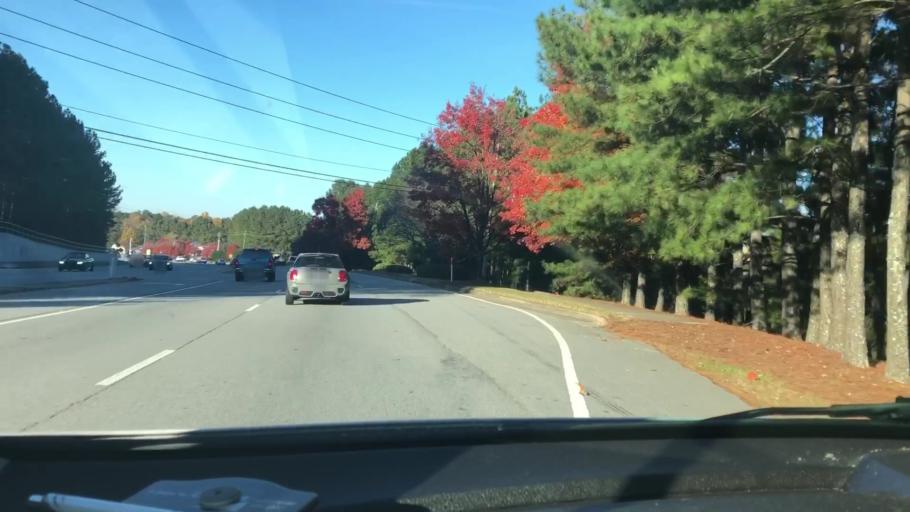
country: US
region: Georgia
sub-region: Gwinnett County
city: Berkeley Lake
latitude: 33.9950
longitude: -84.1677
